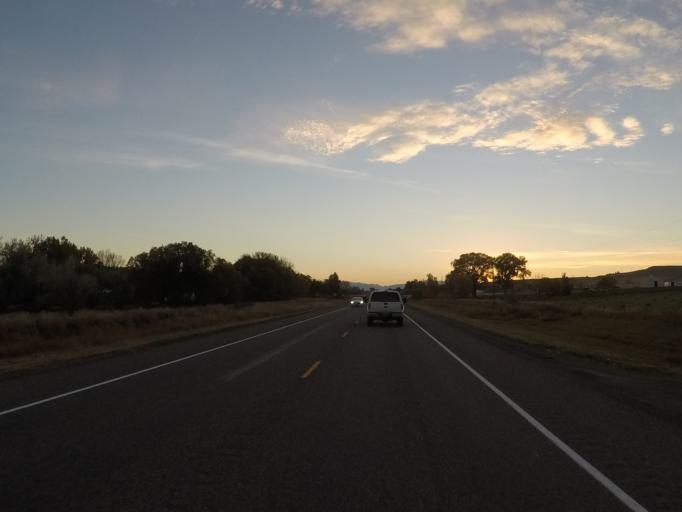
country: US
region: Montana
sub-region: Yellowstone County
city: Laurel
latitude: 45.5104
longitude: -108.8996
